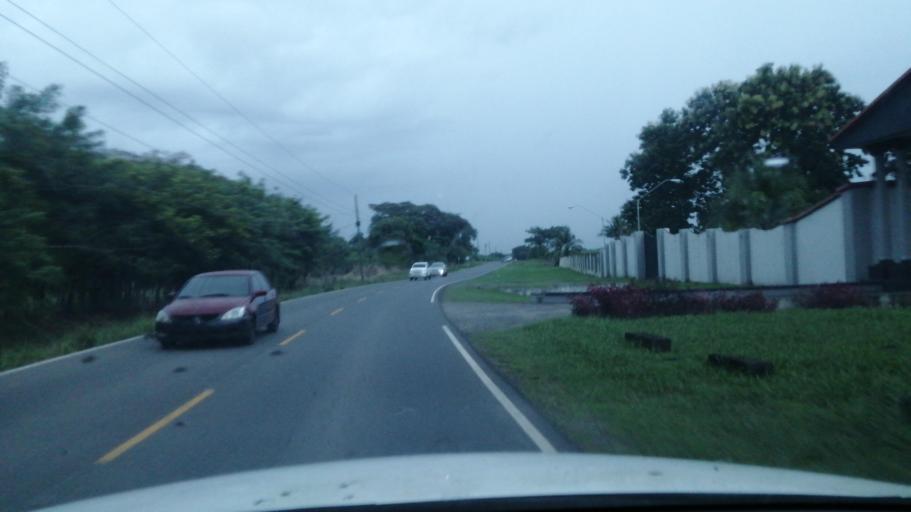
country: PA
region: Chiriqui
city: Pedregal
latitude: 8.3977
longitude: -82.4825
